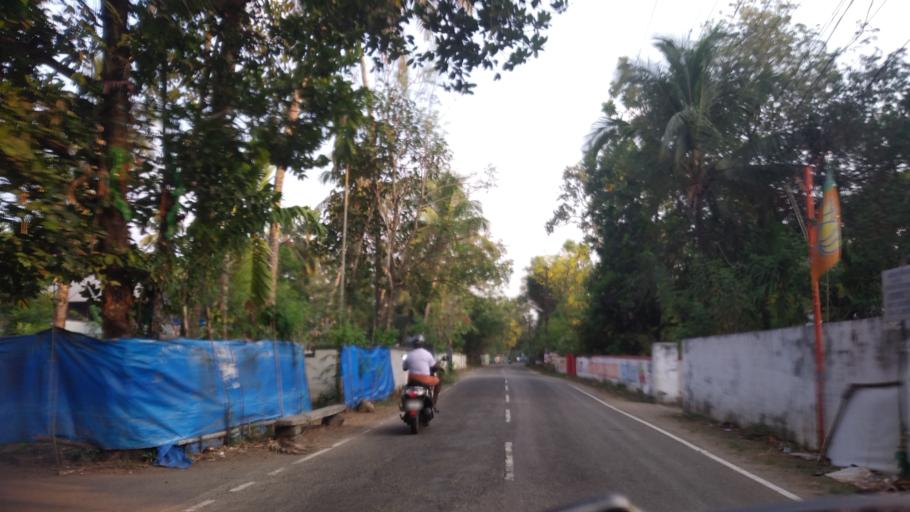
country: IN
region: Kerala
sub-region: Thrissur District
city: Thanniyam
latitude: 10.3751
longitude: 76.1033
